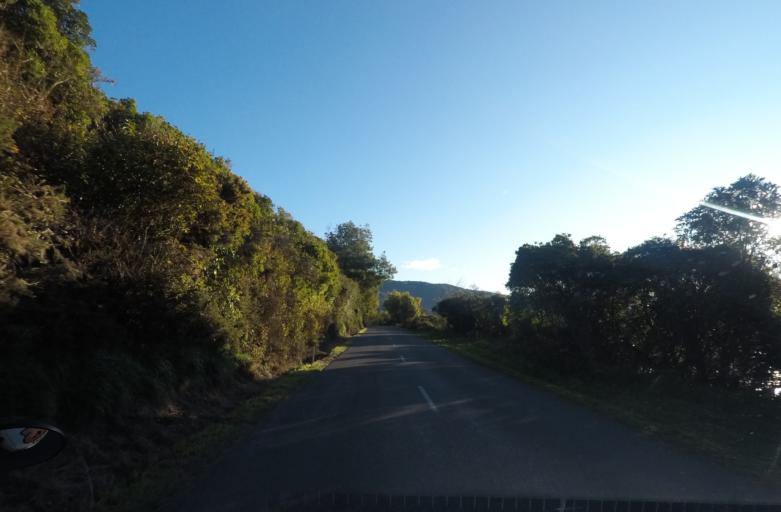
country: NZ
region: Marlborough
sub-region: Marlborough District
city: Picton
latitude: -41.2926
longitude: 173.8399
